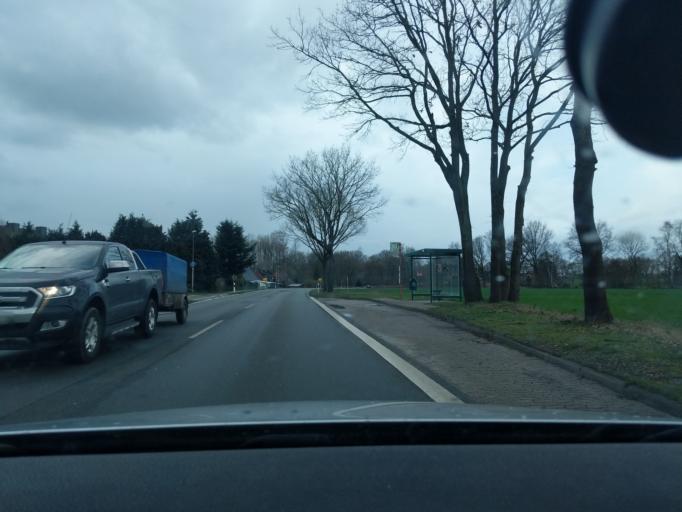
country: DE
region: Lower Saxony
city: Kutenholz
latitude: 53.4886
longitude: 9.3193
